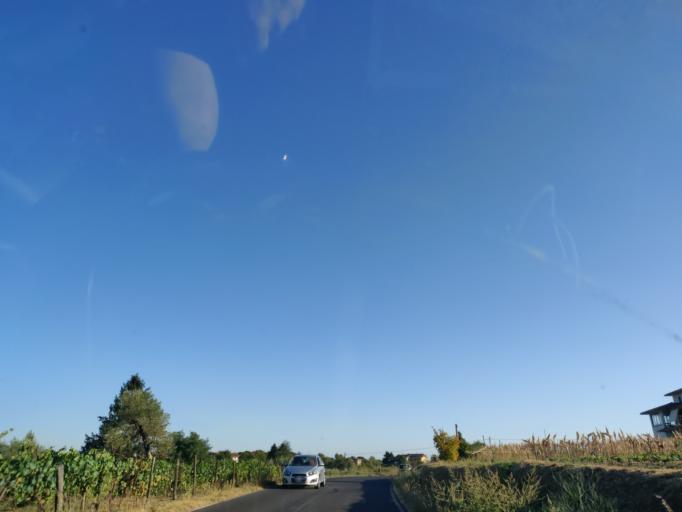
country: IT
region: Latium
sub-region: Provincia di Viterbo
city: Acquapendente
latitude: 42.7356
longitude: 11.8771
